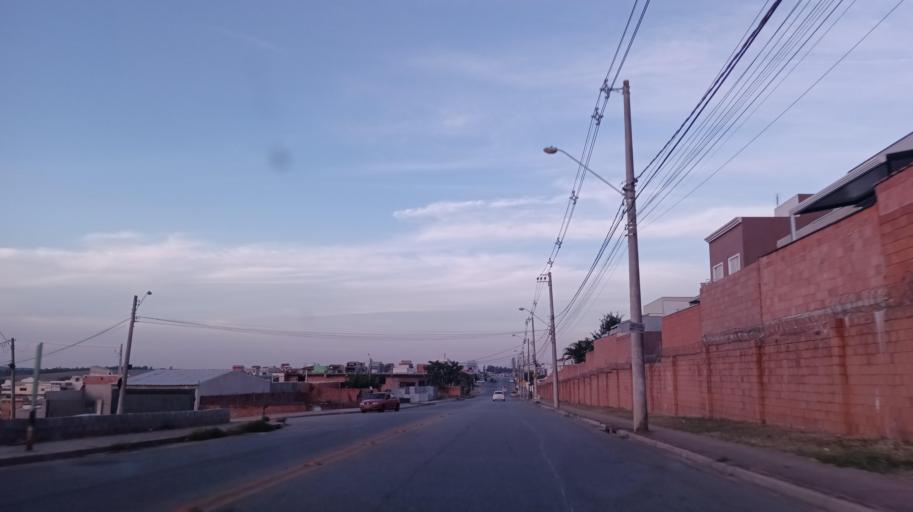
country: BR
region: Sao Paulo
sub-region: Sorocaba
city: Sorocaba
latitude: -23.4423
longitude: -47.5044
